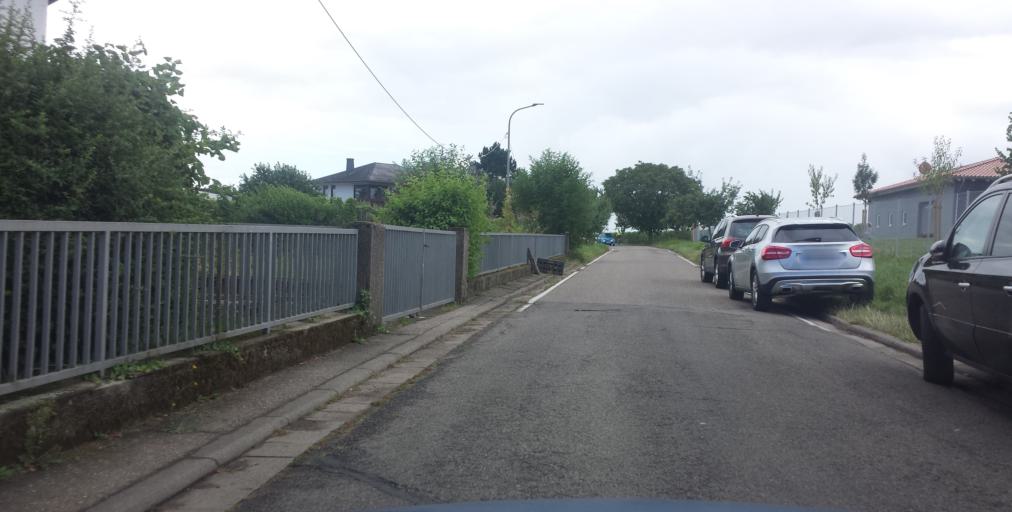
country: DE
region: Rheinland-Pfalz
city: Hainfeld
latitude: 49.2548
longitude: 8.1022
